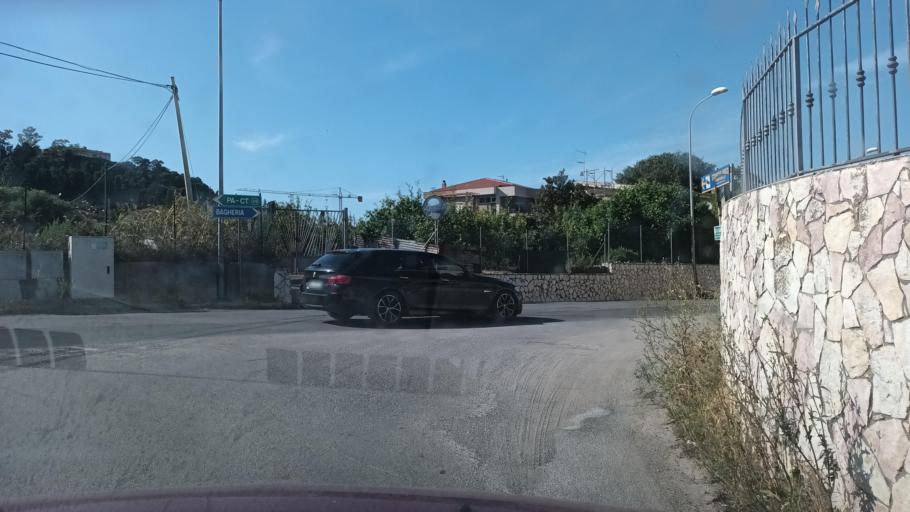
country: IT
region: Sicily
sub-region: Palermo
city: Bagheria
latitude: 38.0667
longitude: 13.5181
